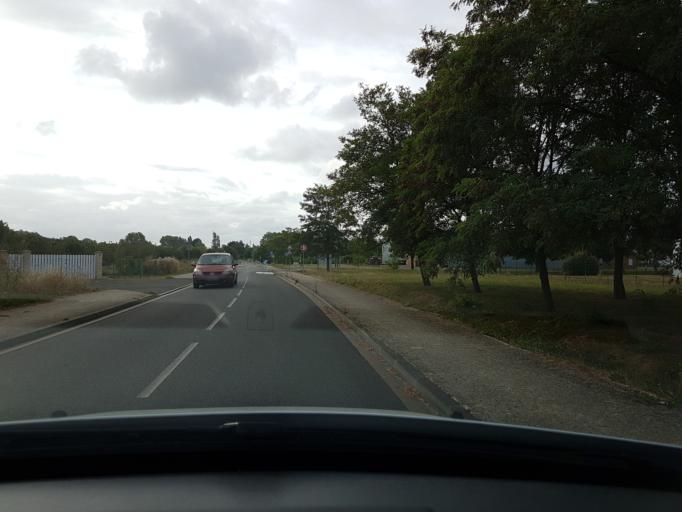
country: FR
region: Centre
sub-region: Departement d'Indre-et-Loire
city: Larcay
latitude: 47.3505
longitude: 0.7711
